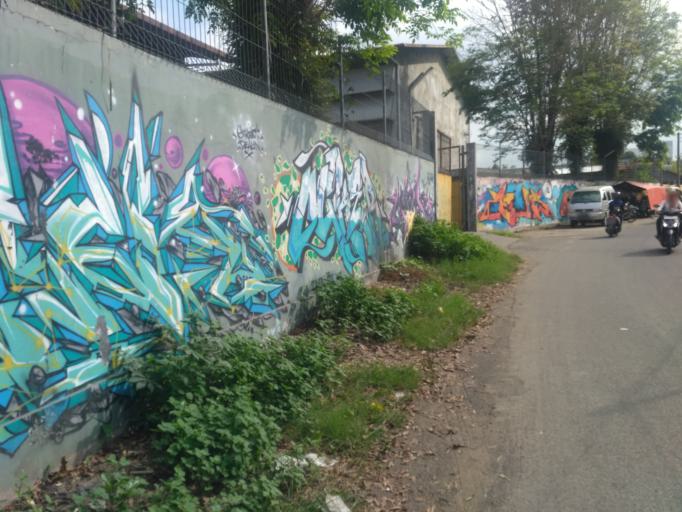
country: ID
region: Daerah Istimewa Yogyakarta
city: Yogyakarta
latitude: -7.7628
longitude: 110.3586
